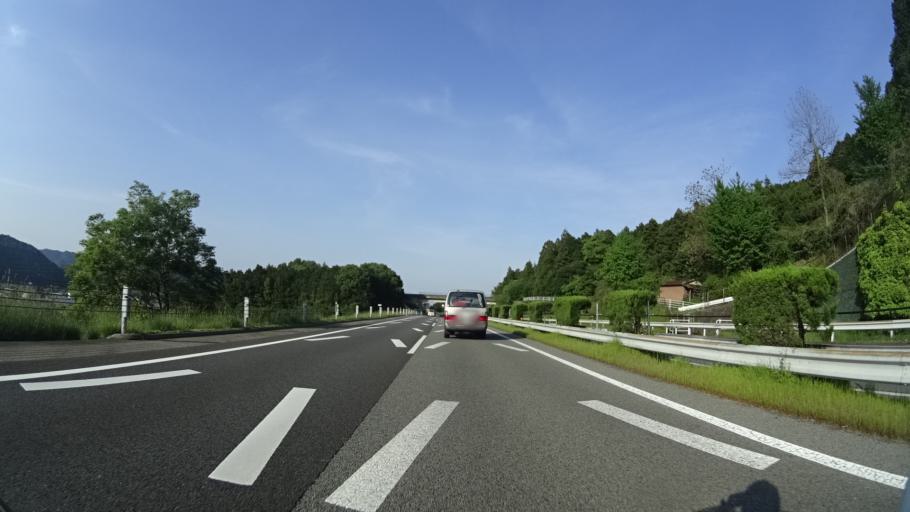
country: JP
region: Ehime
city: Niihama
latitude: 33.9376
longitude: 133.3805
